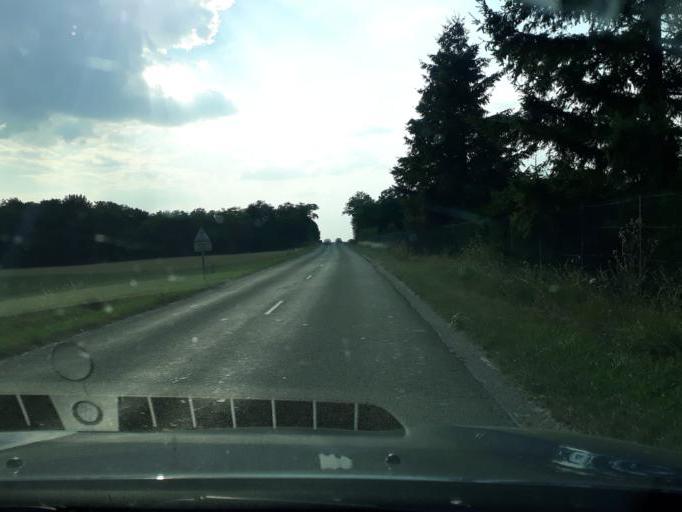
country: FR
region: Centre
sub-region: Departement du Loiret
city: Baule
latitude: 47.8478
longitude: 1.6395
